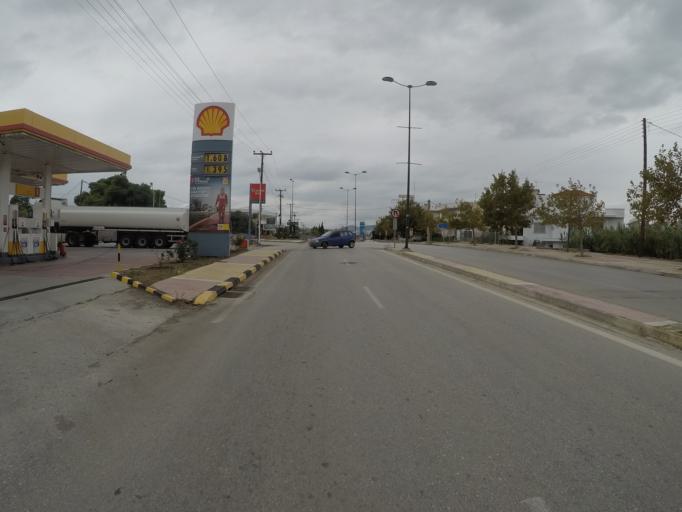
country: GR
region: Peloponnese
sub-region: Nomos Korinthias
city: Loutraki
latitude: 37.9541
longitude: 22.9795
